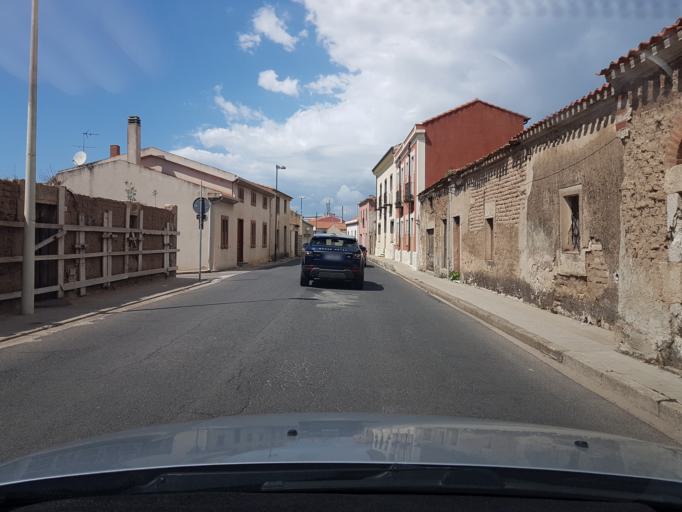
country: IT
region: Sardinia
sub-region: Provincia di Oristano
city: Riola Sardo
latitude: 39.9934
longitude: 8.5414
